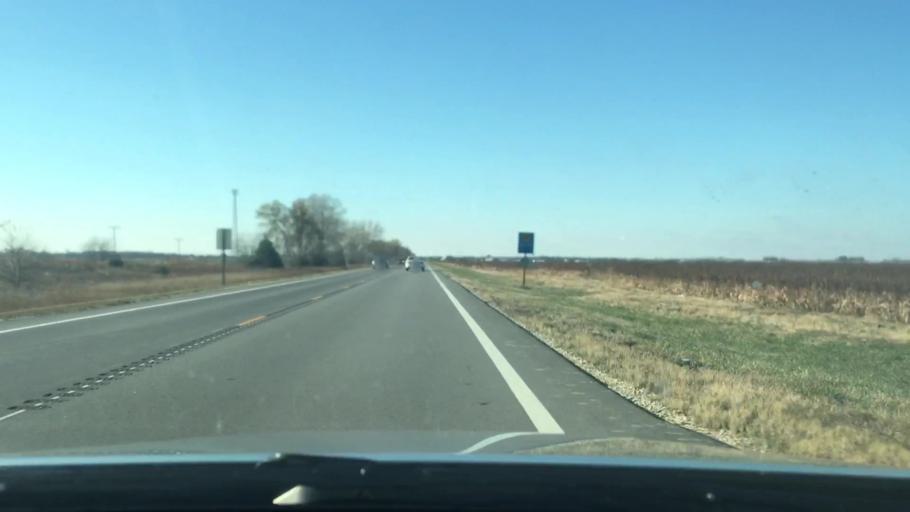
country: US
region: Kansas
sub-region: Reno County
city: Nickerson
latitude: 38.1248
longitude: -98.0506
